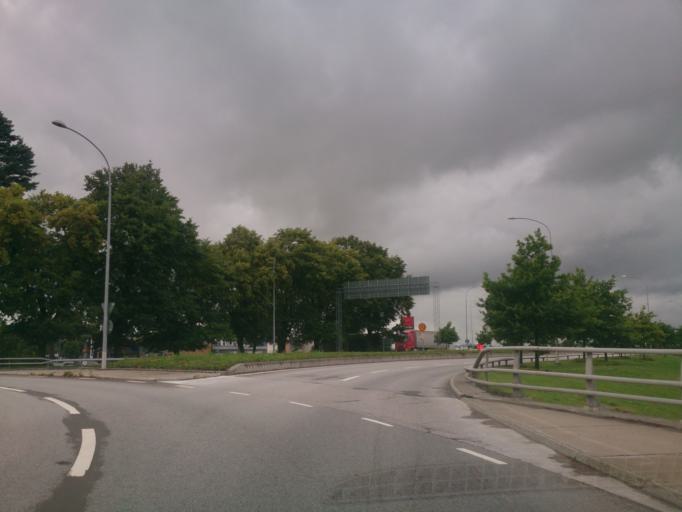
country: SE
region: OEstergoetland
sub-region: Linkopings Kommun
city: Linkoping
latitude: 58.4308
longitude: 15.5862
